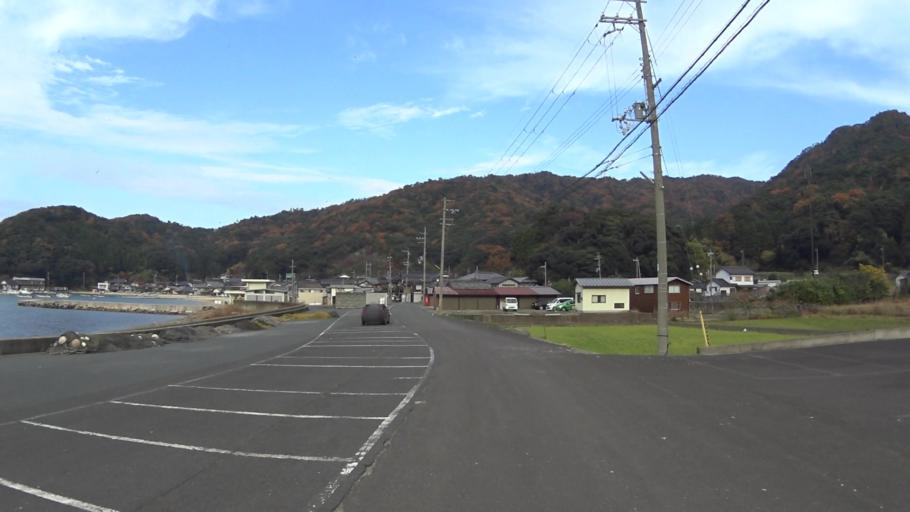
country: JP
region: Kyoto
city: Maizuru
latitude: 35.5670
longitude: 135.4275
